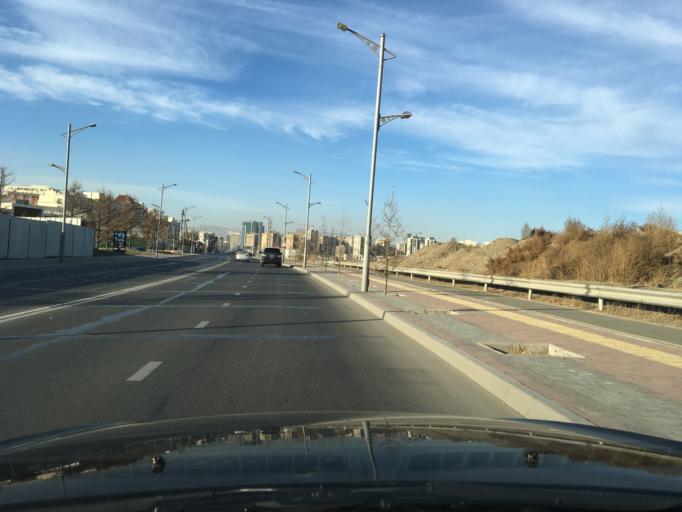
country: MN
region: Ulaanbaatar
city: Ulaanbaatar
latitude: 47.8911
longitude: 106.9382
